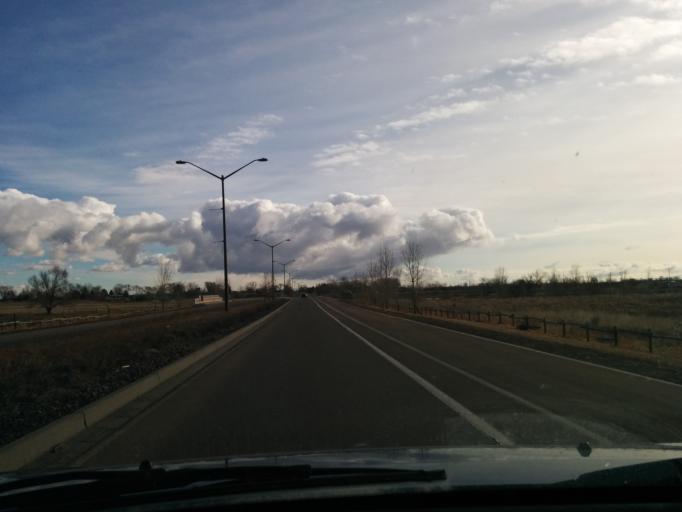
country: US
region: Colorado
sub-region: Larimer County
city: Fort Collins
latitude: 40.5669
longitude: -105.0220
